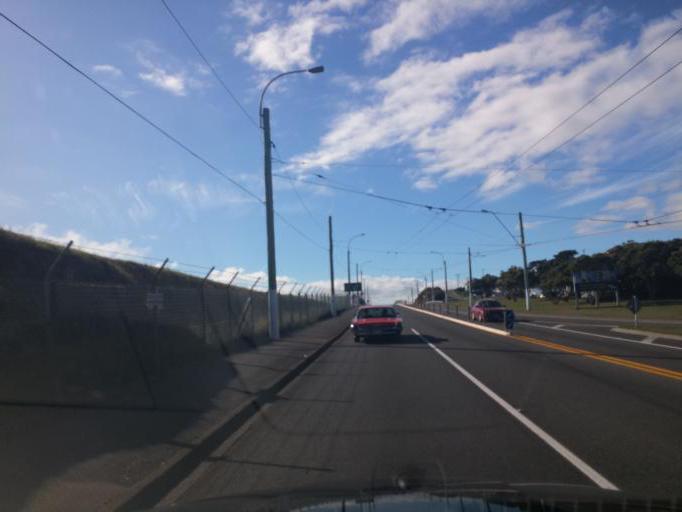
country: NZ
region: Wellington
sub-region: Wellington City
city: Wellington
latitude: -41.3207
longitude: 174.8092
